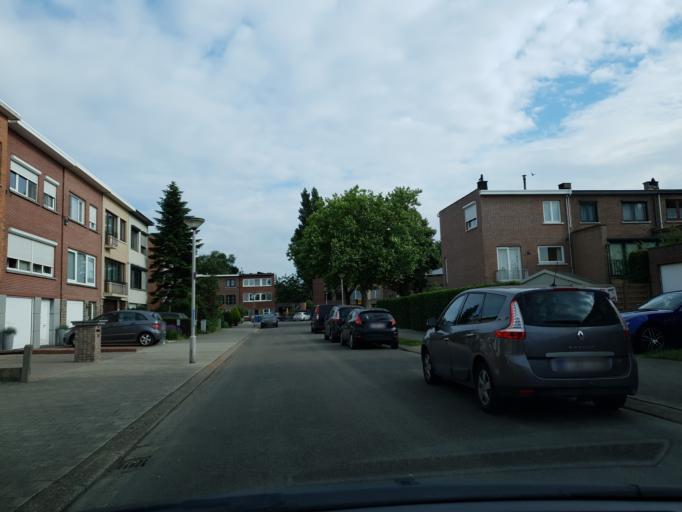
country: BE
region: Flanders
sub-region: Provincie Antwerpen
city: Kapellen
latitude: 51.2768
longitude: 4.4433
